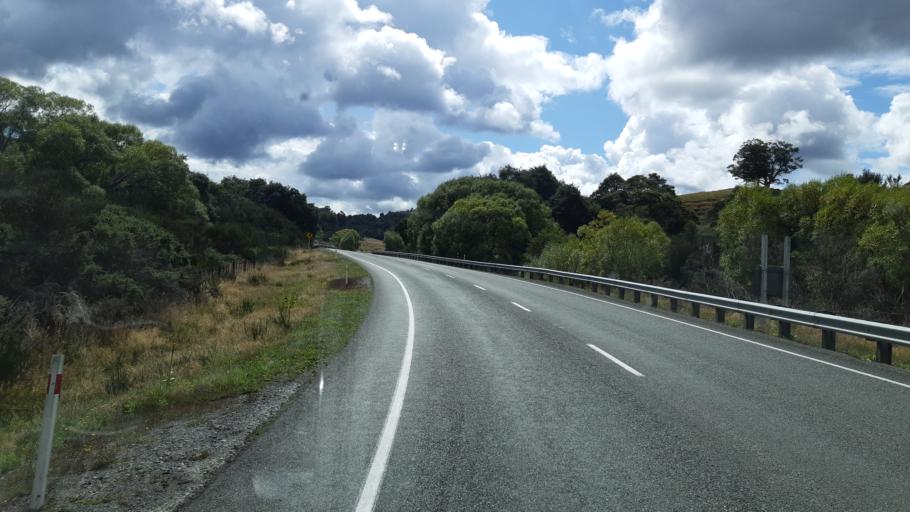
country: NZ
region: Tasman
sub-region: Tasman District
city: Wakefield
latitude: -41.6449
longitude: 172.6587
